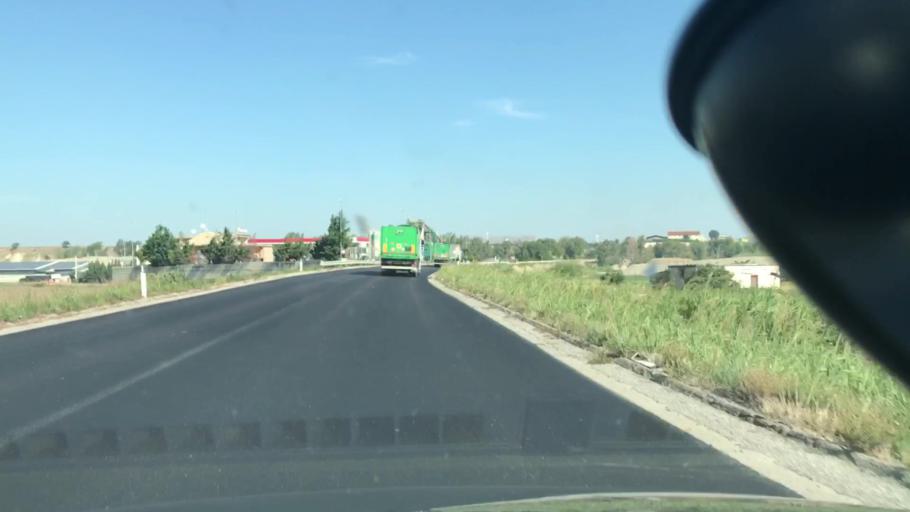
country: IT
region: Apulia
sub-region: Provincia di Foggia
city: Candela
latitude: 41.0923
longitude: 15.5946
